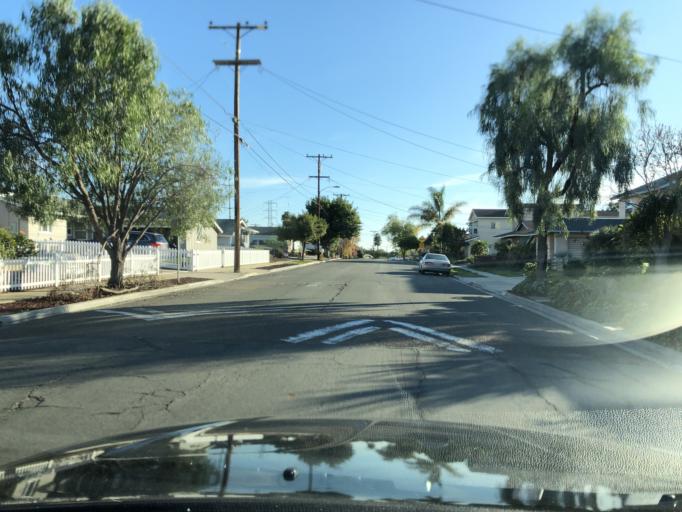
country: US
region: California
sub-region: San Diego County
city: La Jolla
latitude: 32.8204
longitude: -117.1853
